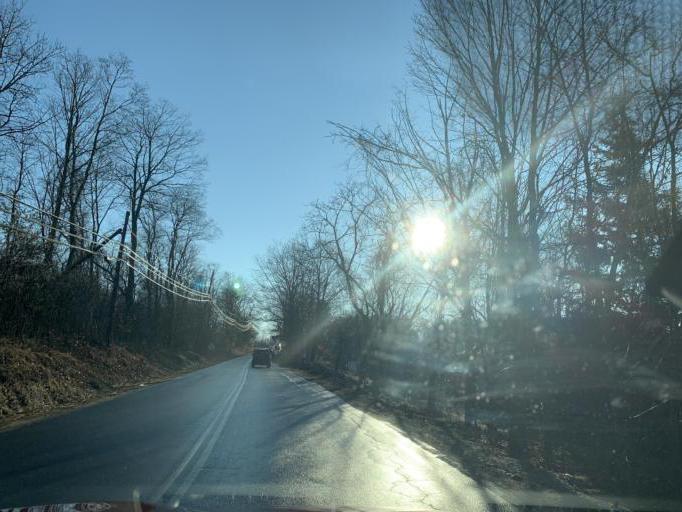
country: US
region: New Hampshire
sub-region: Rockingham County
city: Londonderry
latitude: 42.8741
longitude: -71.3603
